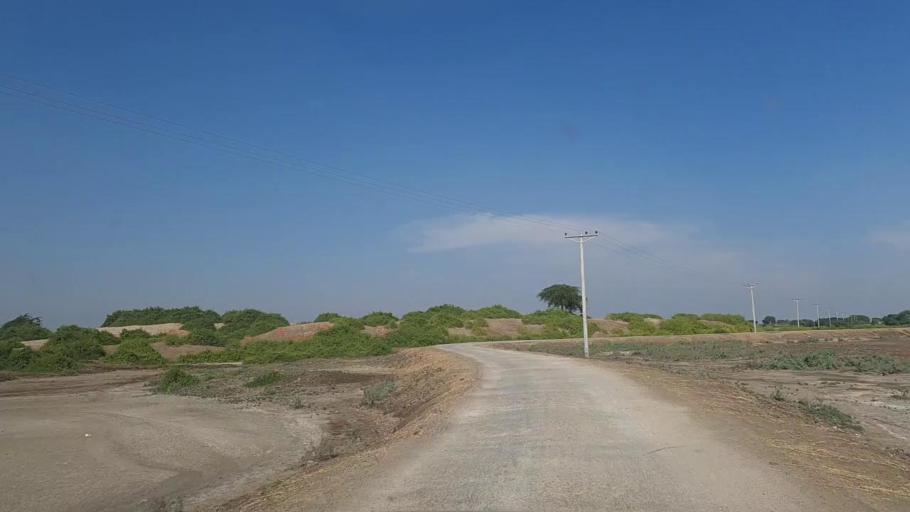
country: PK
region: Sindh
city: Mirpur Batoro
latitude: 24.7466
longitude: 68.2767
